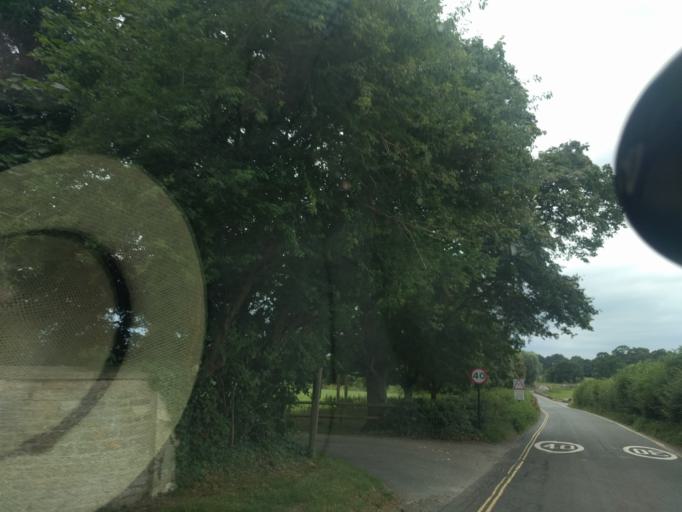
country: GB
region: England
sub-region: Wiltshire
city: Lacock
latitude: 51.4117
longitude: -2.1094
